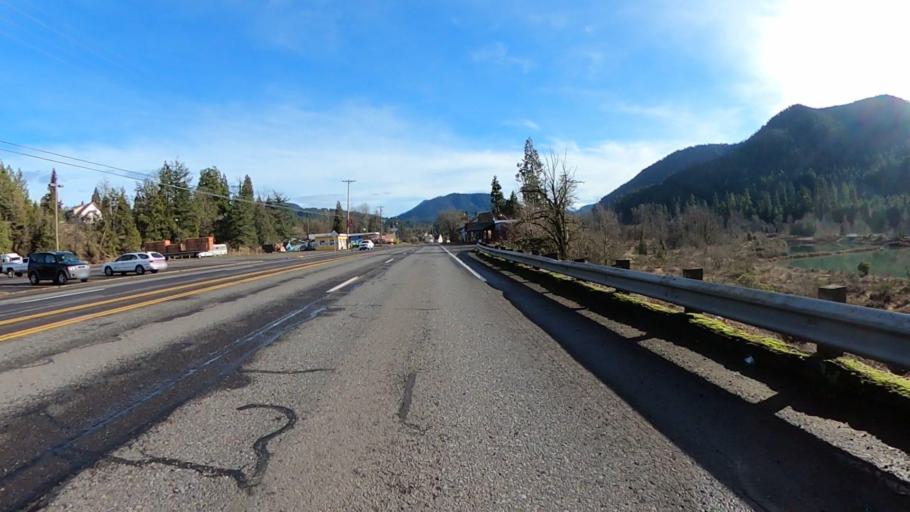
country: US
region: Oregon
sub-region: Lane County
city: Oakridge
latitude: 43.7444
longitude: -122.4669
